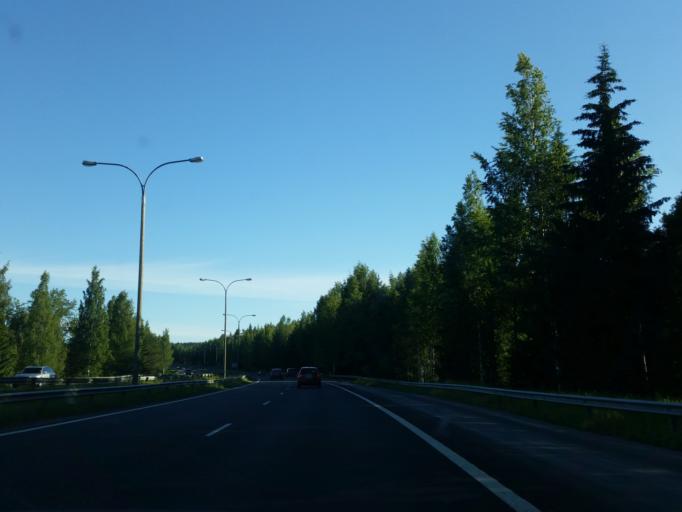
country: FI
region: Northern Savo
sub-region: Kuopio
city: Kuopio
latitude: 62.8755
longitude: 27.6224
